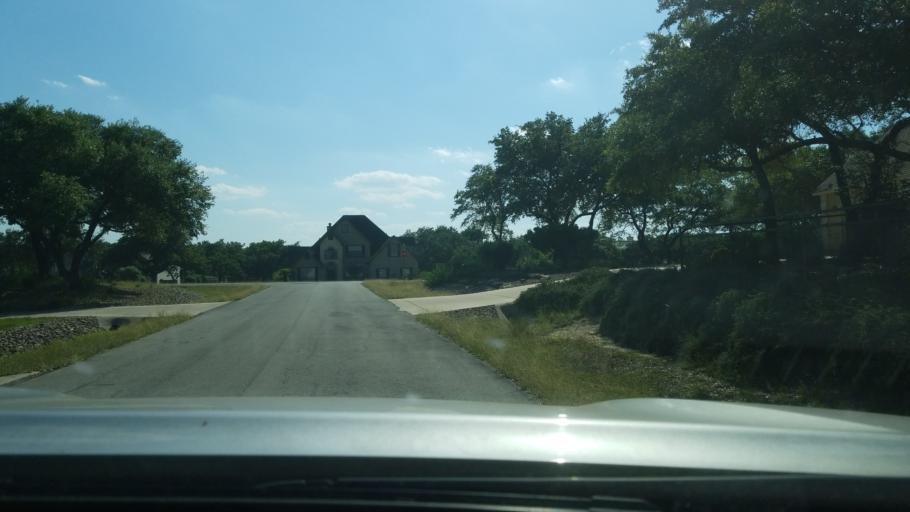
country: US
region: Texas
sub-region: Comal County
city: Bulverde
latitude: 29.8318
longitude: -98.4033
